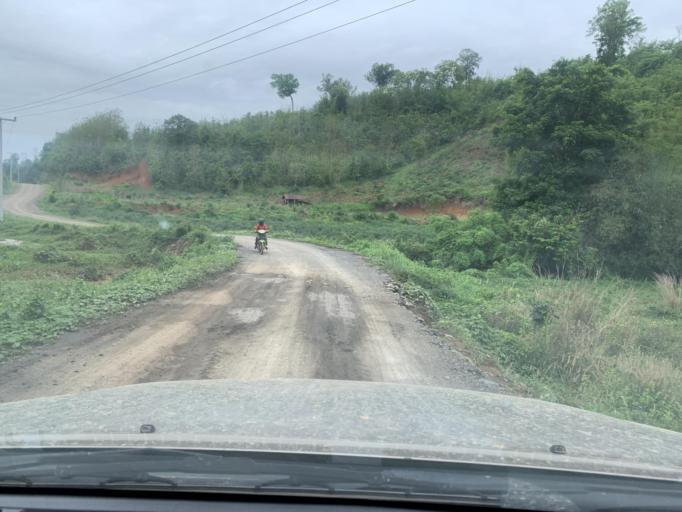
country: TH
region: Nan
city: Mae Charim
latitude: 18.4180
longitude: 101.4619
